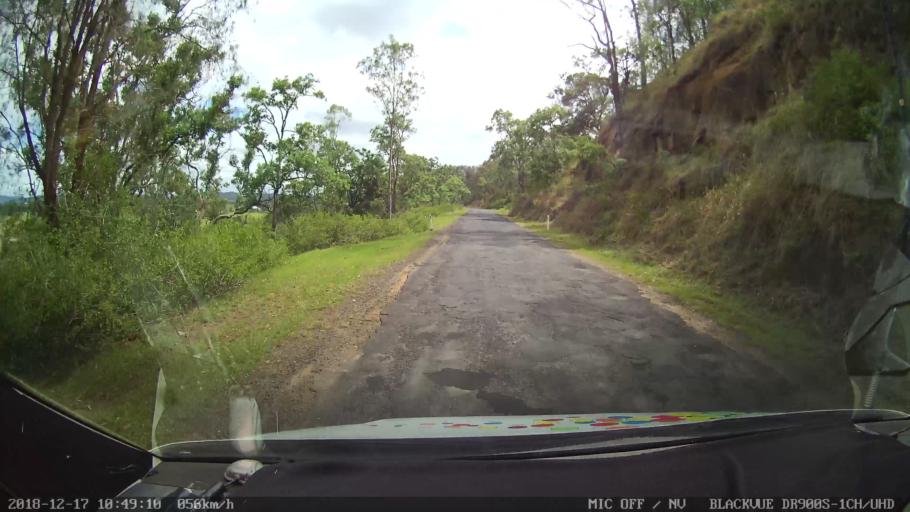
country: AU
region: New South Wales
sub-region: Clarence Valley
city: Gordon
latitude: -28.8677
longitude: 152.5724
